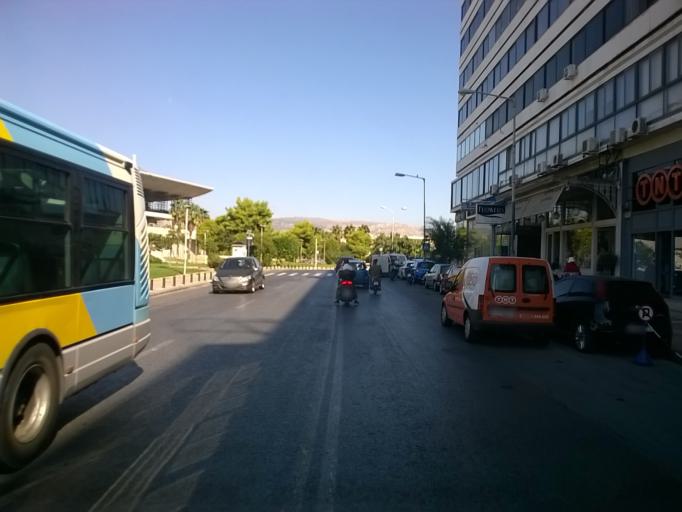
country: GR
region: Attica
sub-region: Nomos Attikis
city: Piraeus
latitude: 37.9379
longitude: 23.6394
